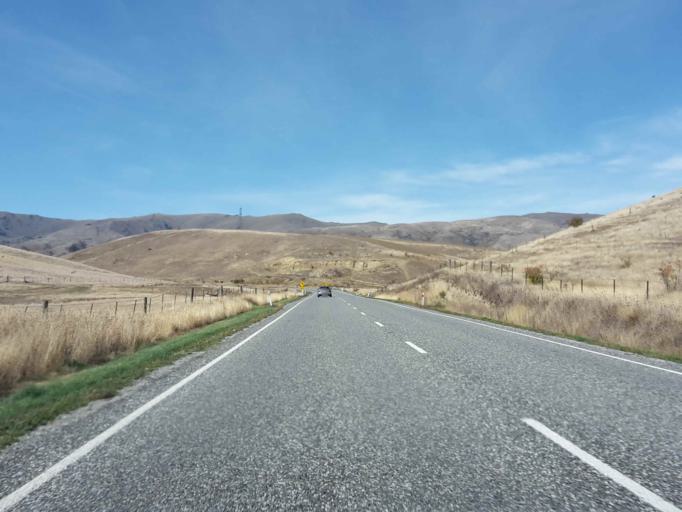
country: NZ
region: Otago
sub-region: Queenstown-Lakes District
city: Wanaka
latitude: -44.8072
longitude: 169.4862
